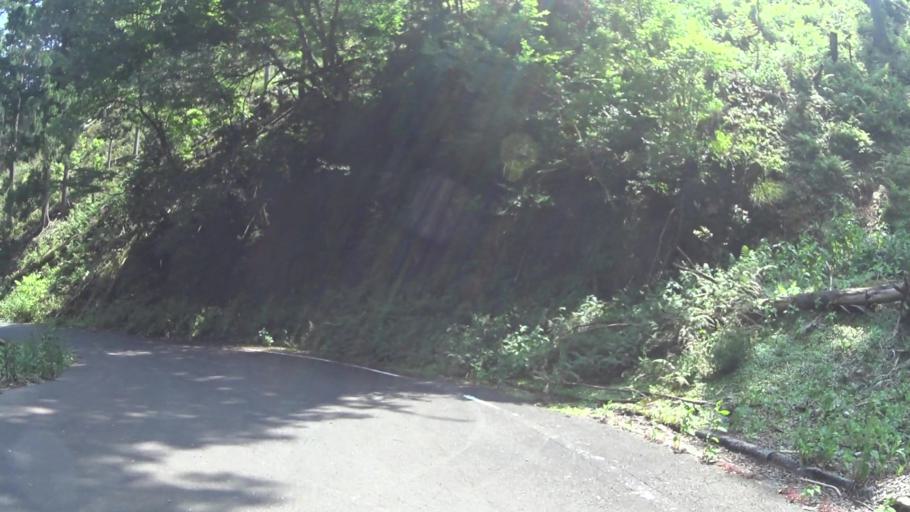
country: JP
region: Kyoto
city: Maizuru
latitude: 35.3516
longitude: 135.5163
